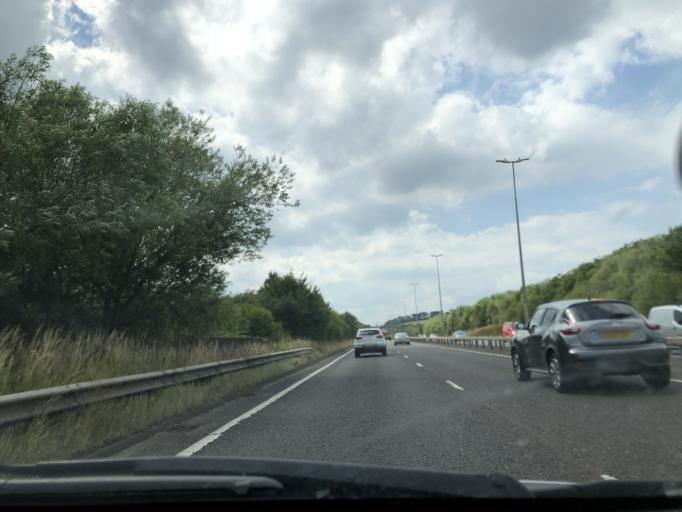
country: GB
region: England
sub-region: Kent
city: Tankerton
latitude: 51.3388
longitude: 1.0462
